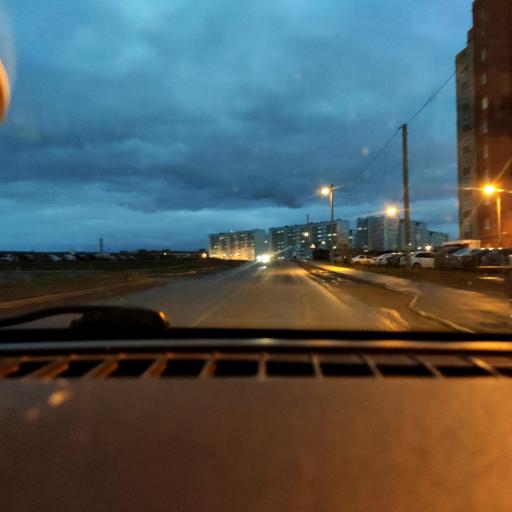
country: RU
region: Perm
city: Froly
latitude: 57.9224
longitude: 56.2731
